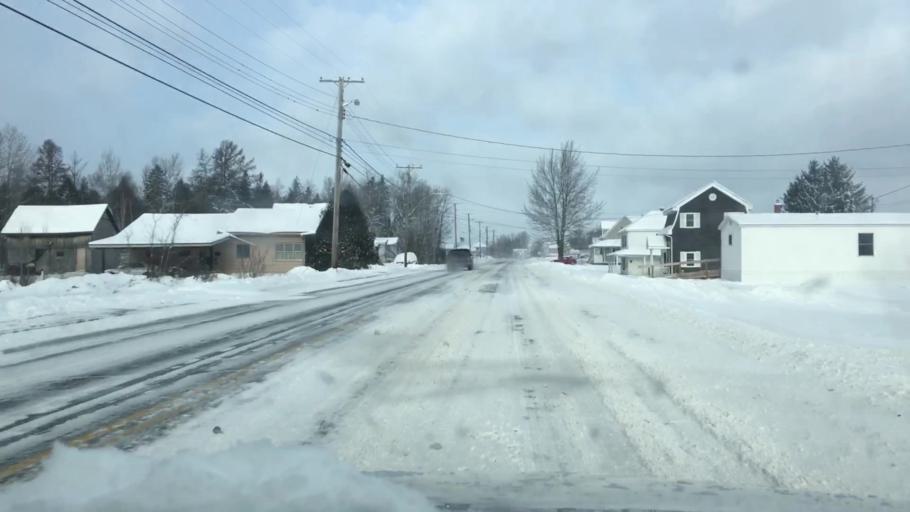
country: US
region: Maine
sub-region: Aroostook County
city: Van Buren
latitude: 47.1820
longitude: -67.9530
